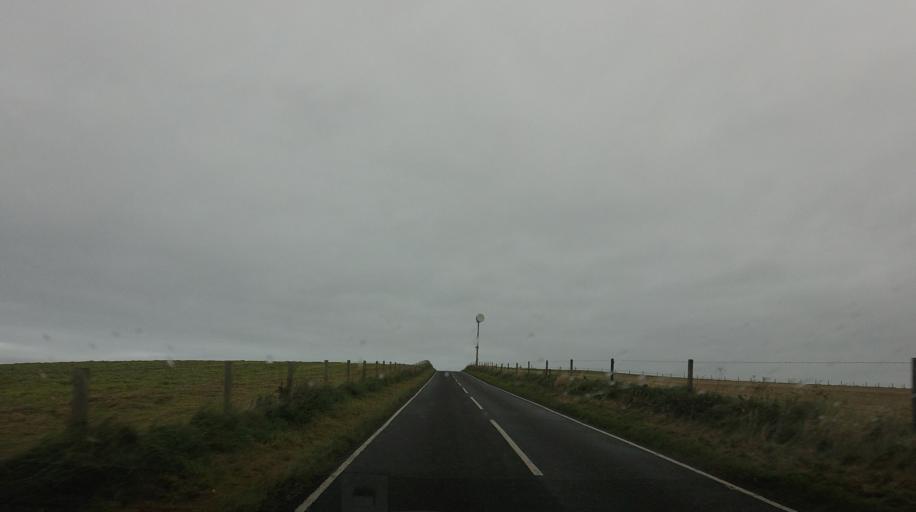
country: GB
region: Scotland
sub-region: Orkney Islands
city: Stromness
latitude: 59.1289
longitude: -3.3026
